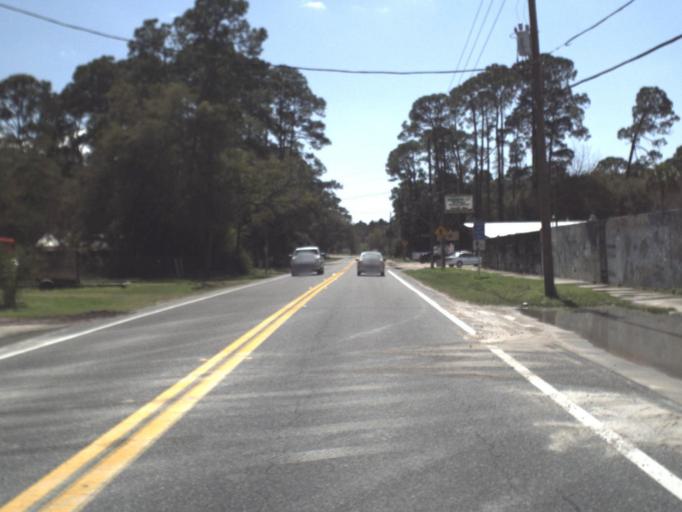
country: US
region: Florida
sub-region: Wakulla County
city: Crawfordville
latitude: 30.0362
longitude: -84.3886
